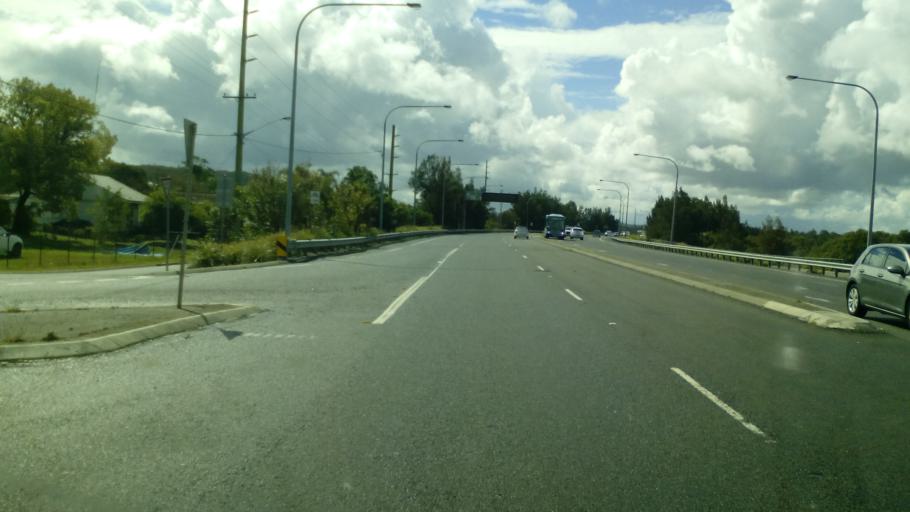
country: AU
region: New South Wales
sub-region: Lake Macquarie Shire
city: Fennell Bay
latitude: -32.9662
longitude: 151.6077
